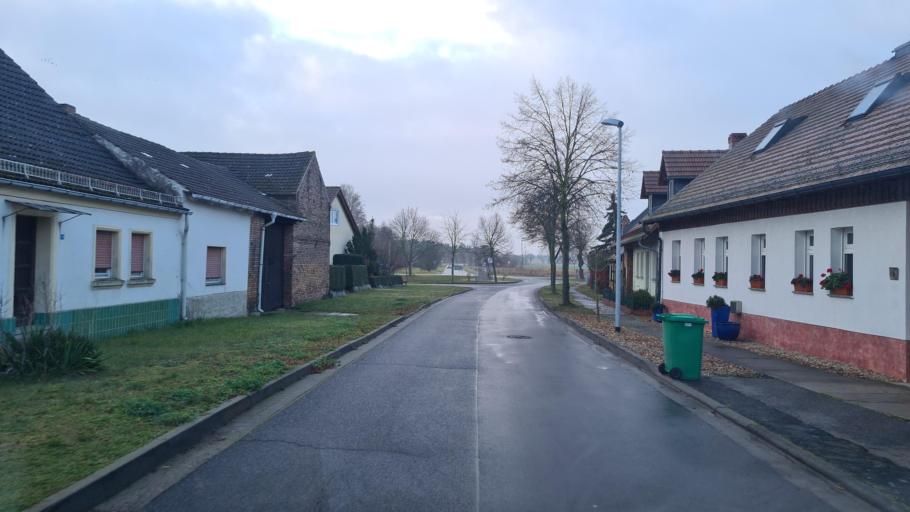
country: DE
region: Brandenburg
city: Beelitz
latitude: 52.1398
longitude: 12.9899
